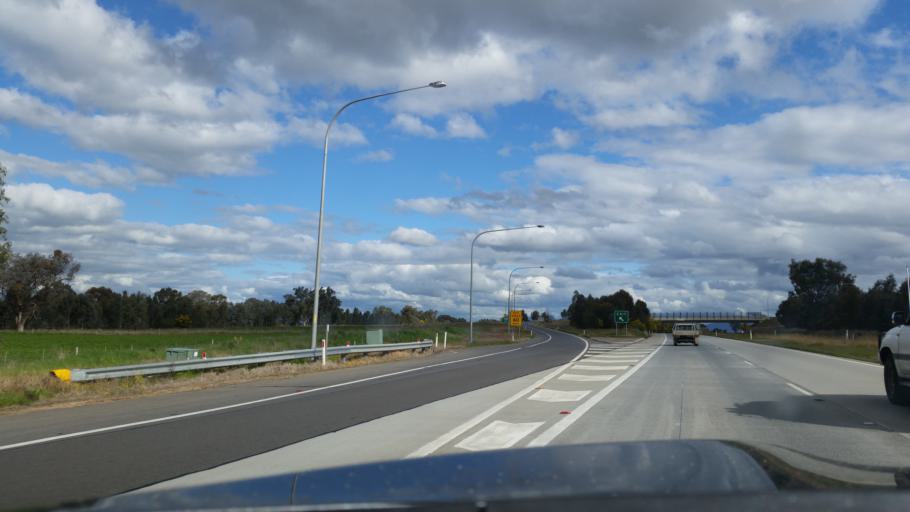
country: AU
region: New South Wales
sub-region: Albury Municipality
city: Lavington
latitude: -35.9984
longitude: 146.9927
